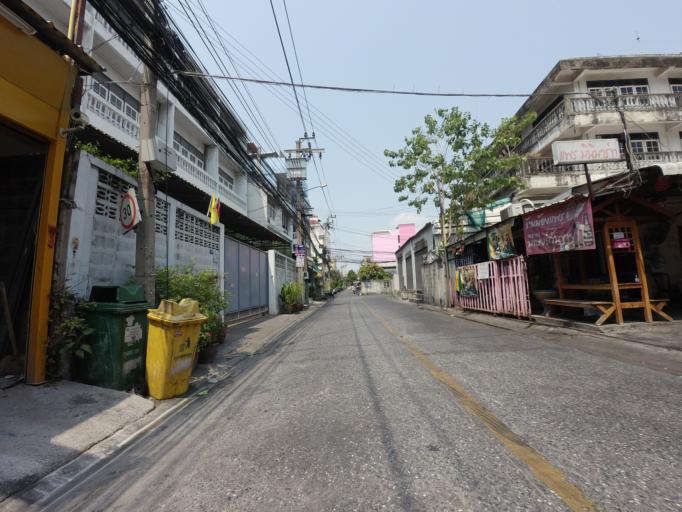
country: TH
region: Bangkok
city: Din Daeng
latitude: 13.7636
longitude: 100.5610
